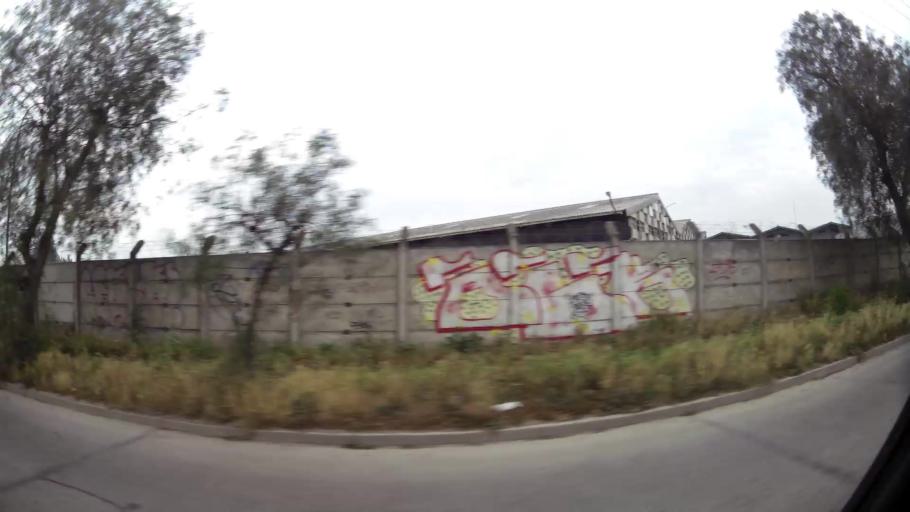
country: CL
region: Santiago Metropolitan
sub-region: Provincia de Santiago
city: Lo Prado
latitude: -33.4821
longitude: -70.7041
